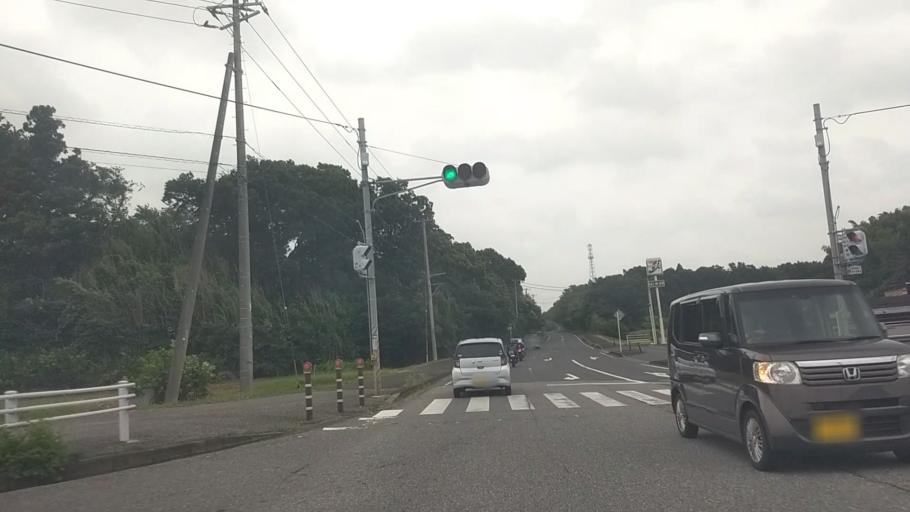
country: JP
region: Chiba
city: Kisarazu
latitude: 35.3885
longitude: 139.9896
